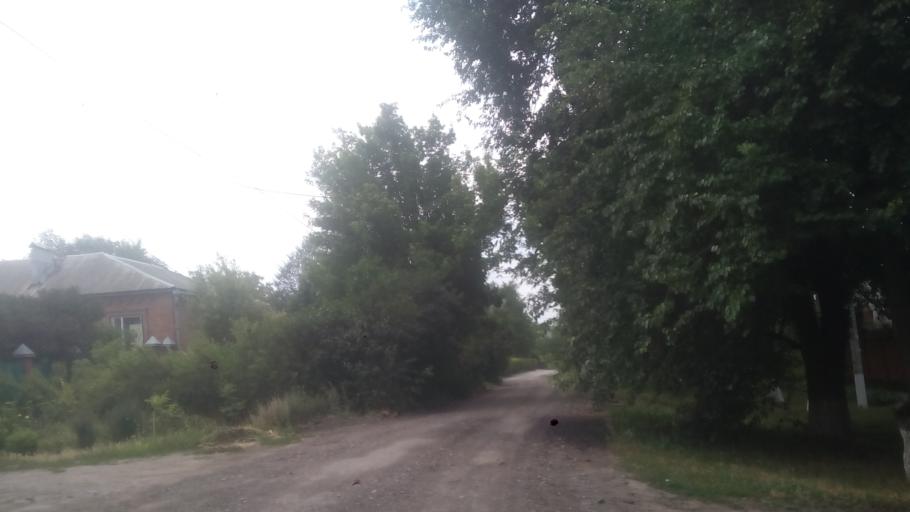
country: RU
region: Rostov
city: Rostov-na-Donu
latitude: 47.2194
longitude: 39.6507
